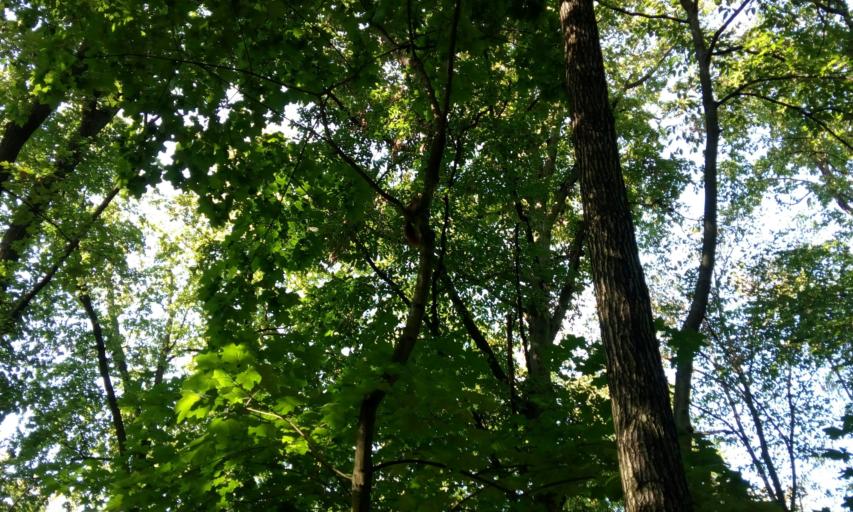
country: PL
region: Masovian Voivodeship
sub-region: Warszawa
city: Zoliborz
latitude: 52.2888
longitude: 20.9704
